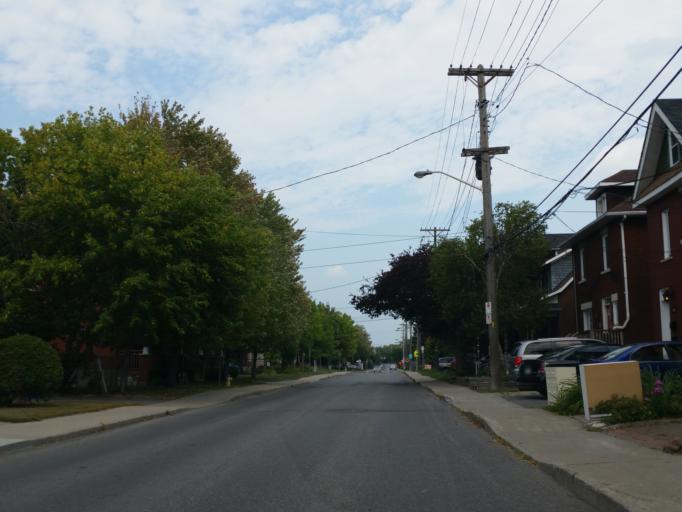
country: CA
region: Ontario
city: Ottawa
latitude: 45.3996
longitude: -75.7273
